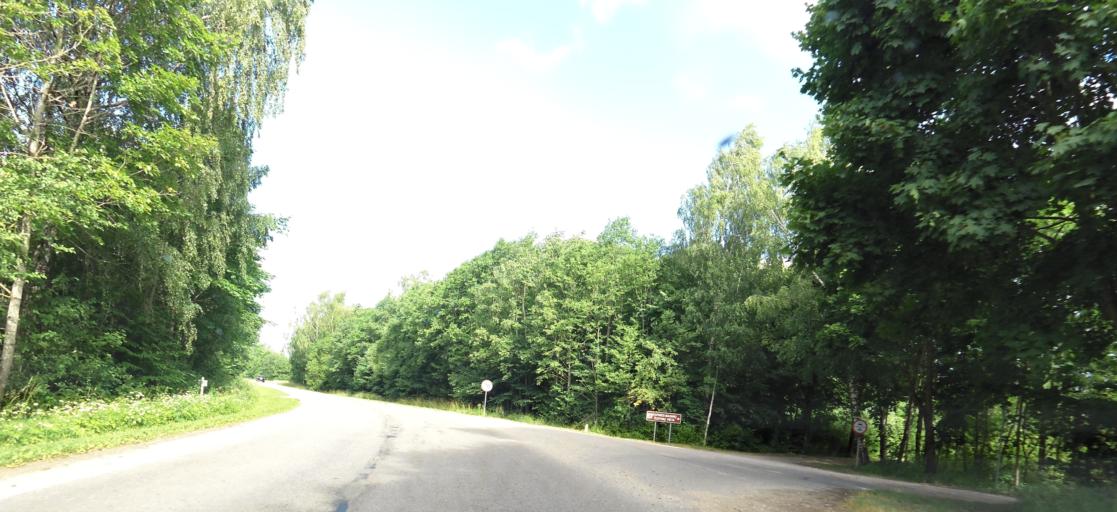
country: LT
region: Panevezys
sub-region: Birzai
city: Birzai
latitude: 56.2208
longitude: 24.7806
